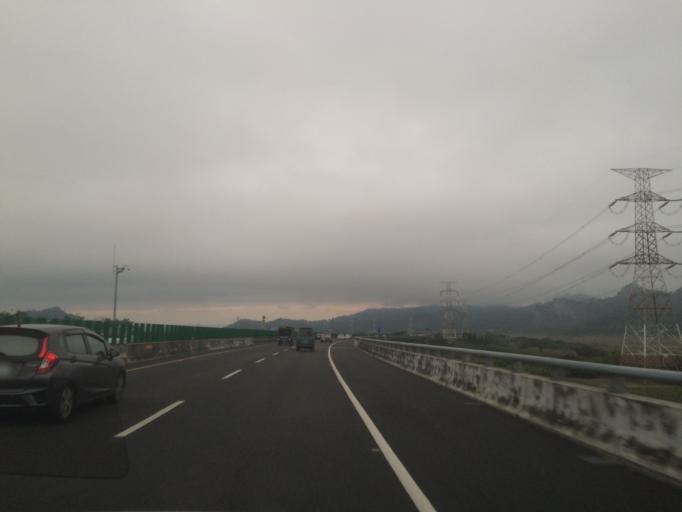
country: TW
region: Taiwan
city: Zhongxing New Village
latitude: 23.9970
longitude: 120.7438
